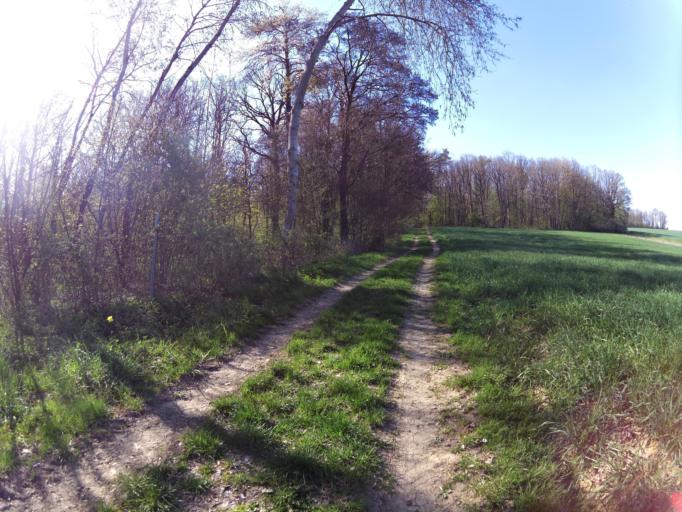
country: DE
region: Bavaria
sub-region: Regierungsbezirk Unterfranken
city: Estenfeld
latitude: 49.8641
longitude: 9.9979
